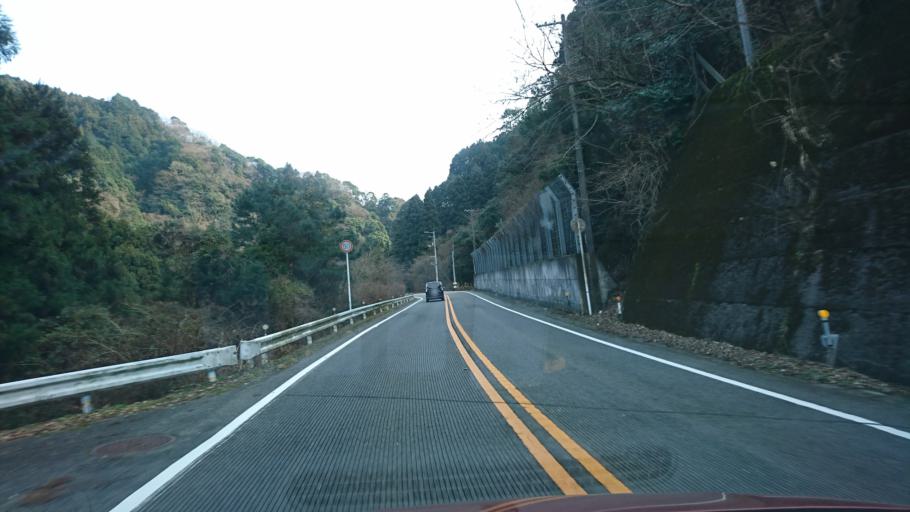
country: JP
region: Ehime
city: Hojo
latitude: 33.9598
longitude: 132.9090
